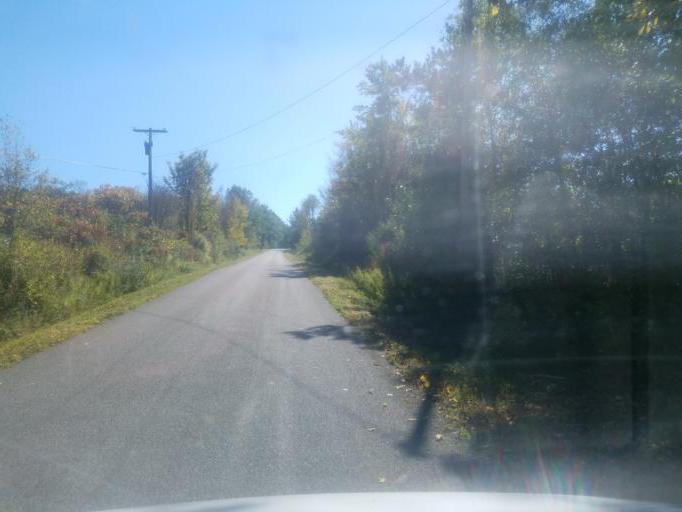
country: US
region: New York
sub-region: Allegany County
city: Houghton
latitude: 42.3192
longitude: -78.2067
